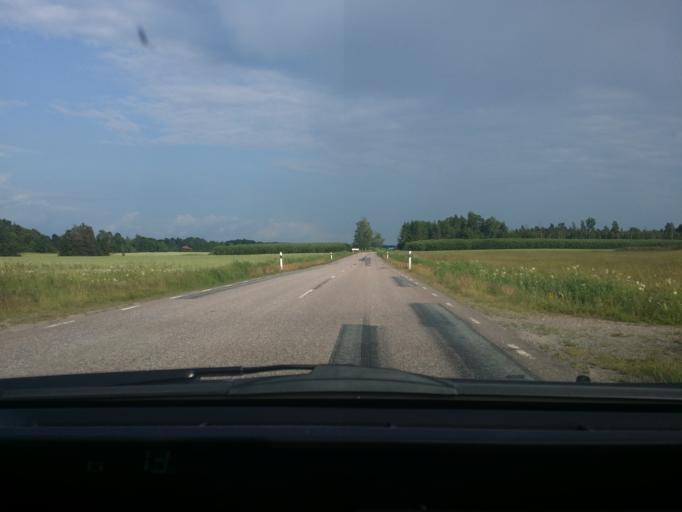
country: SE
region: Vaestmanland
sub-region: Hallstahammars Kommun
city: Kolback
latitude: 59.5610
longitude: 16.3194
